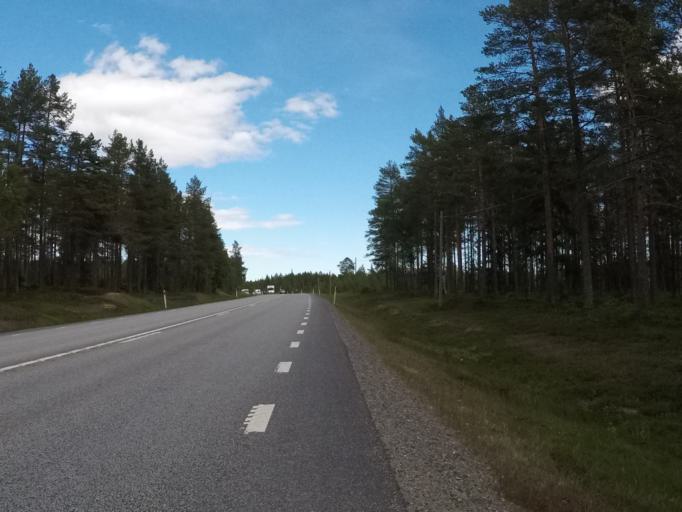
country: SE
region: Vaesterbotten
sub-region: Robertsfors Kommun
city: Robertsfors
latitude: 64.1845
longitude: 20.9897
